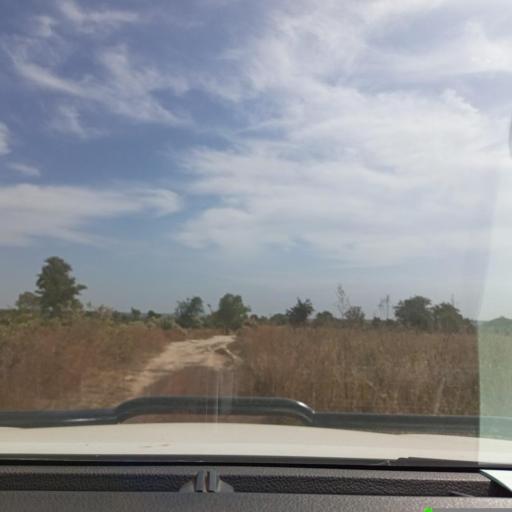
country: ML
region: Koulikoro
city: Kati
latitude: 12.7319
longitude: -8.2541
